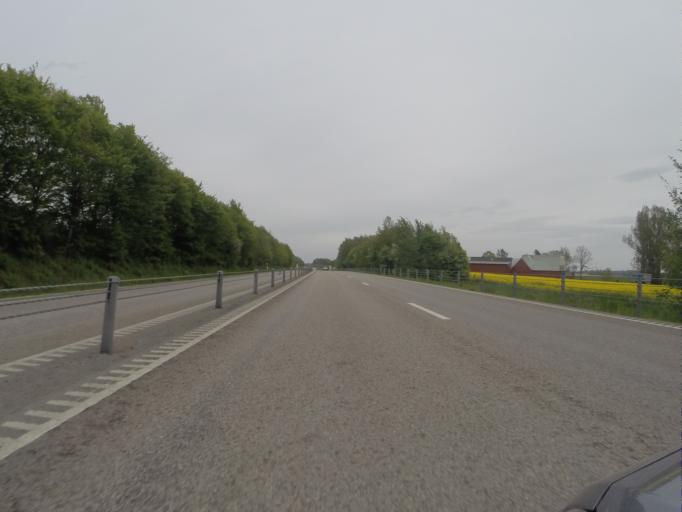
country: SE
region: Skane
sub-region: Bjuvs Kommun
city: Bjuv
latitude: 56.0791
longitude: 12.8952
